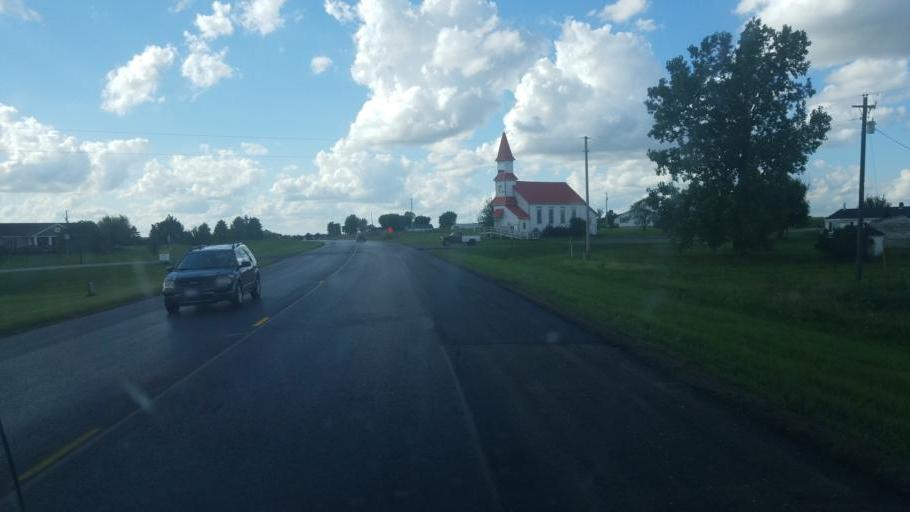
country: US
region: Ohio
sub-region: Hardin County
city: Kenton
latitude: 40.6895
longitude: -83.6915
